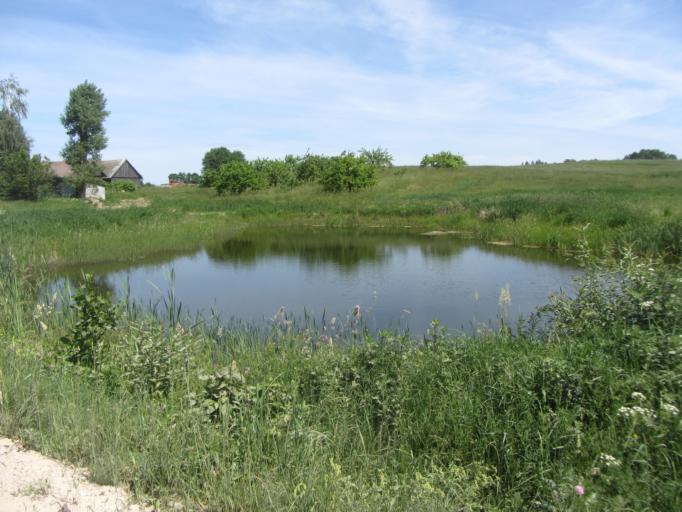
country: LT
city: Jieznas
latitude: 54.6865
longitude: 24.3003
